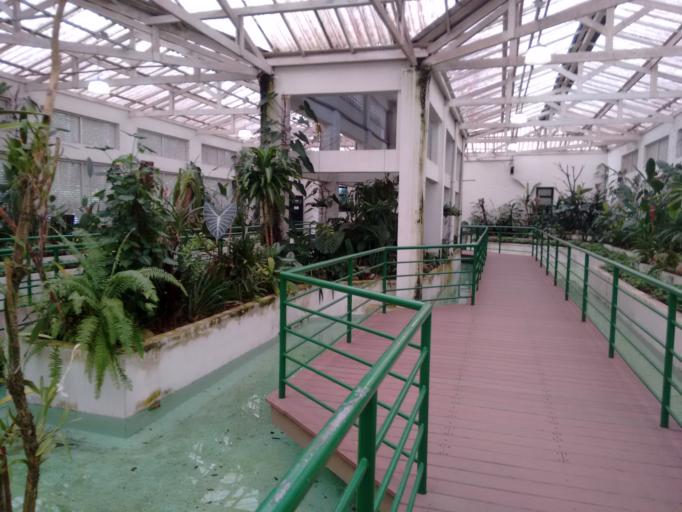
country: BR
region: Sao Paulo
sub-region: Santos
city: Santos
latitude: -23.9654
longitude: -46.3506
